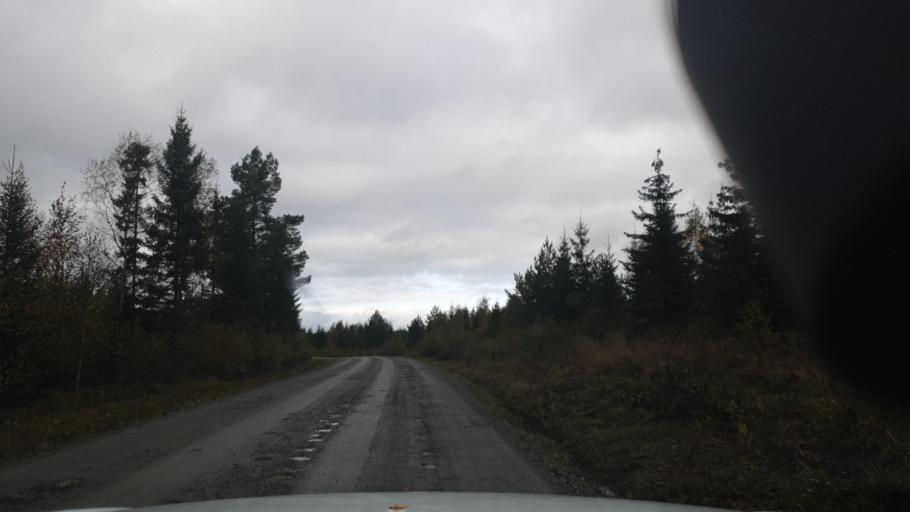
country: SE
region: Vaermland
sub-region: Karlstads Kommun
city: Edsvalla
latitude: 59.4448
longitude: 13.1662
